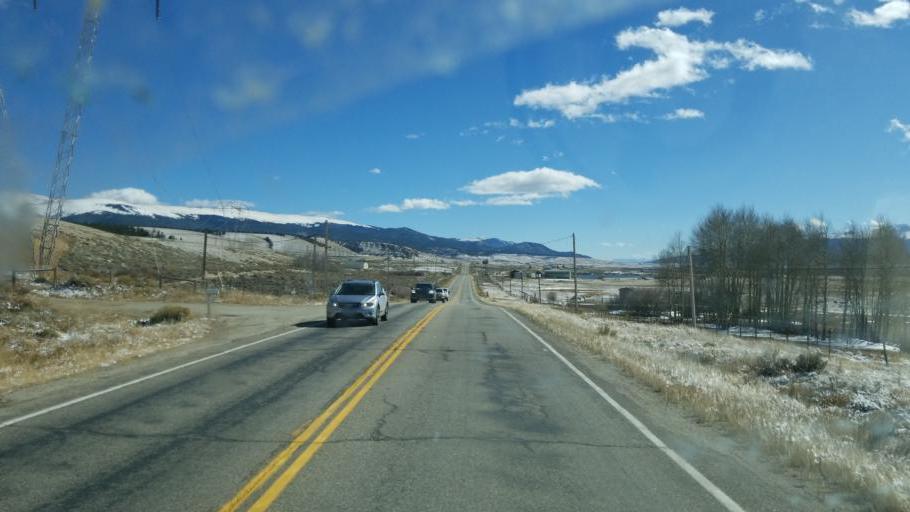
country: US
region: Colorado
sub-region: Lake County
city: Leadville North
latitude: 39.2019
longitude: -106.3426
